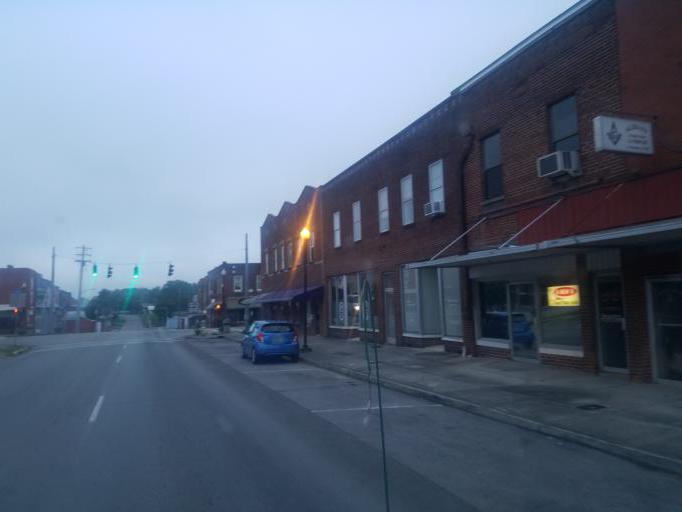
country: US
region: Kentucky
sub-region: Clinton County
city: Albany
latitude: 36.6904
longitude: -85.1352
